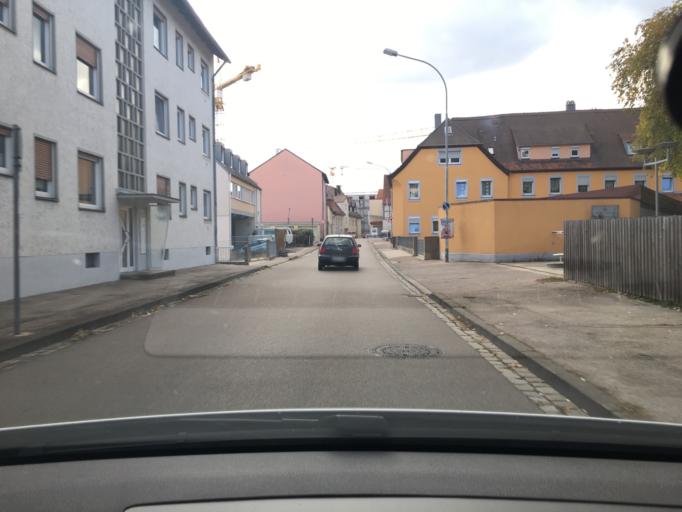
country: DE
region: Bavaria
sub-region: Regierungsbezirk Mittelfranken
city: Ansbach
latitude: 49.3045
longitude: 10.5793
